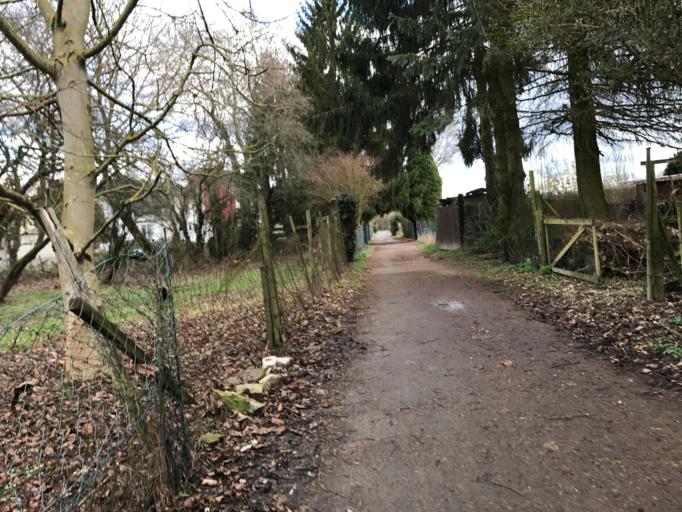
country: DE
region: Hesse
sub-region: Regierungsbezirk Darmstadt
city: Niedernhausen
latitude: 50.0937
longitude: 8.3099
